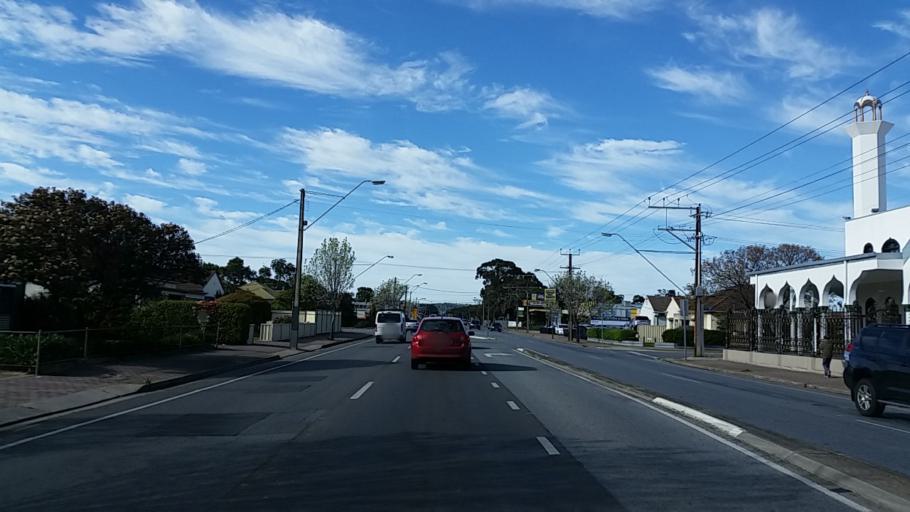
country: AU
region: South Australia
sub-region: Marion
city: South Plympton
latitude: -34.9885
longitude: 138.5566
